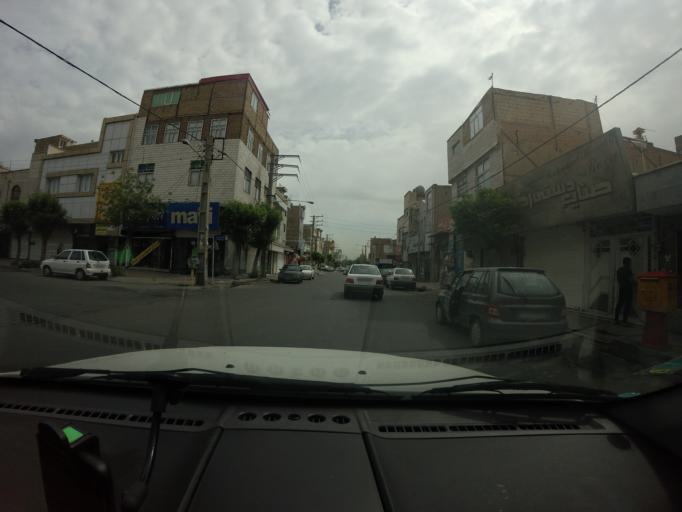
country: IR
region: Tehran
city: Eslamshahr
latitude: 35.5504
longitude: 51.2511
